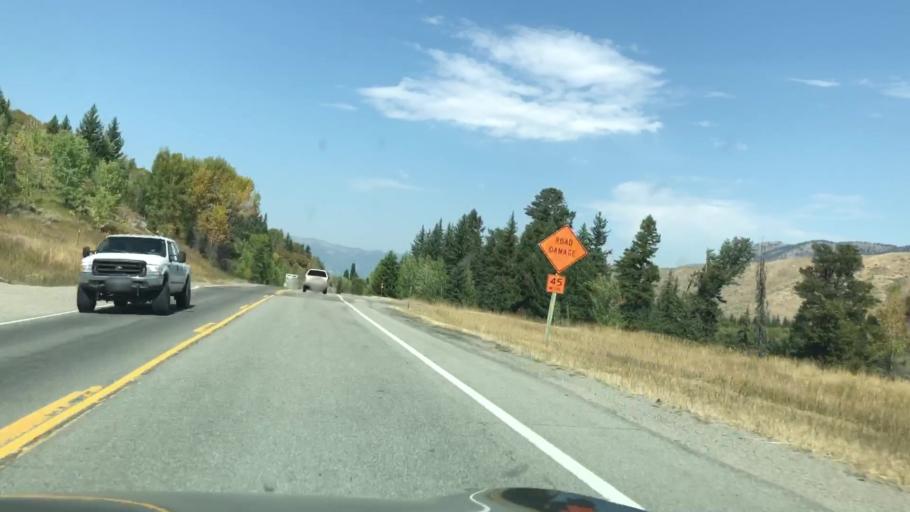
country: US
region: Wyoming
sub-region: Teton County
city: South Park
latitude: 43.3576
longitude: -110.7233
